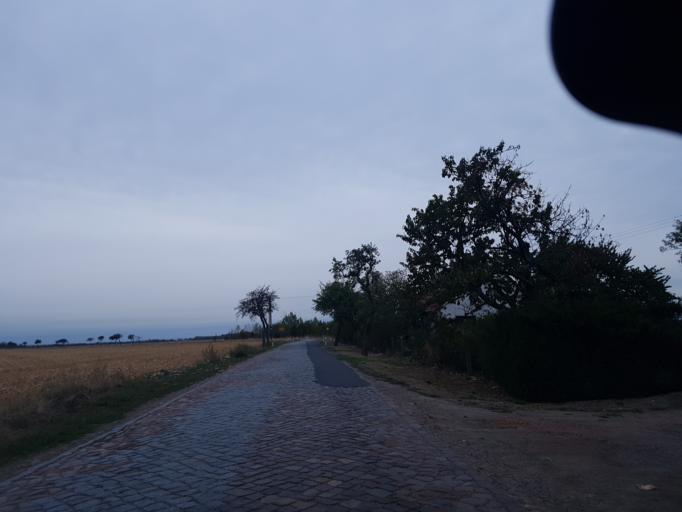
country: DE
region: Saxony
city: Belgern
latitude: 51.4964
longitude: 13.1799
